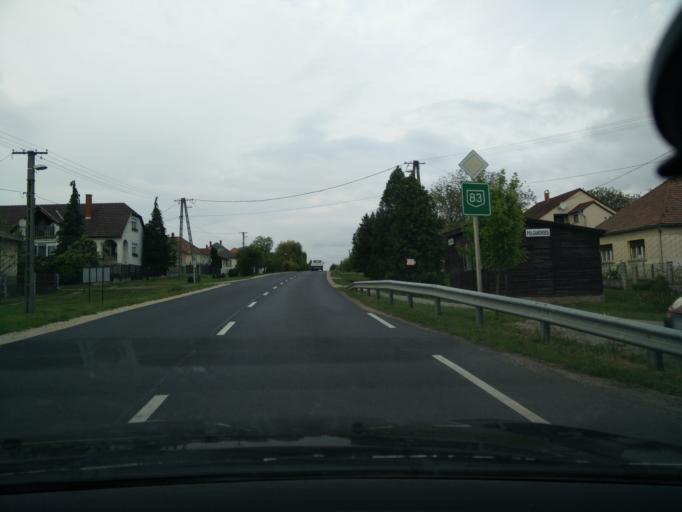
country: HU
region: Gyor-Moson-Sopron
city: Tet
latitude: 47.4613
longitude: 17.4868
